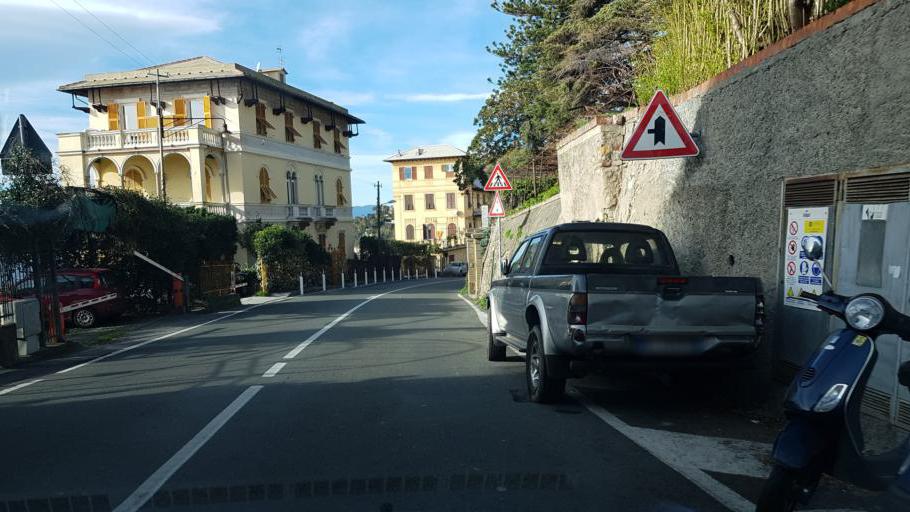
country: IT
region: Liguria
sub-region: Provincia di Genova
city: Sori
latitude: 44.3697
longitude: 9.1070
